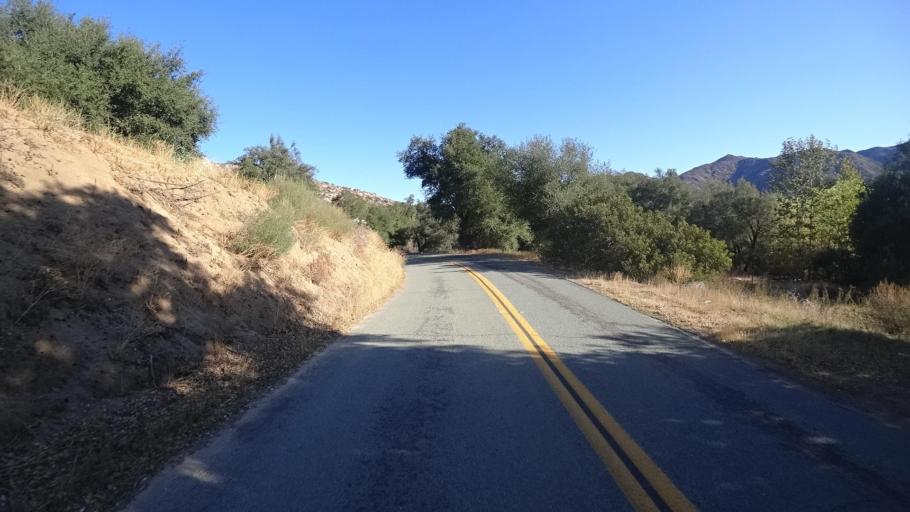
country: MX
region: Baja California
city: Tecate
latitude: 32.6291
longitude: -116.6866
